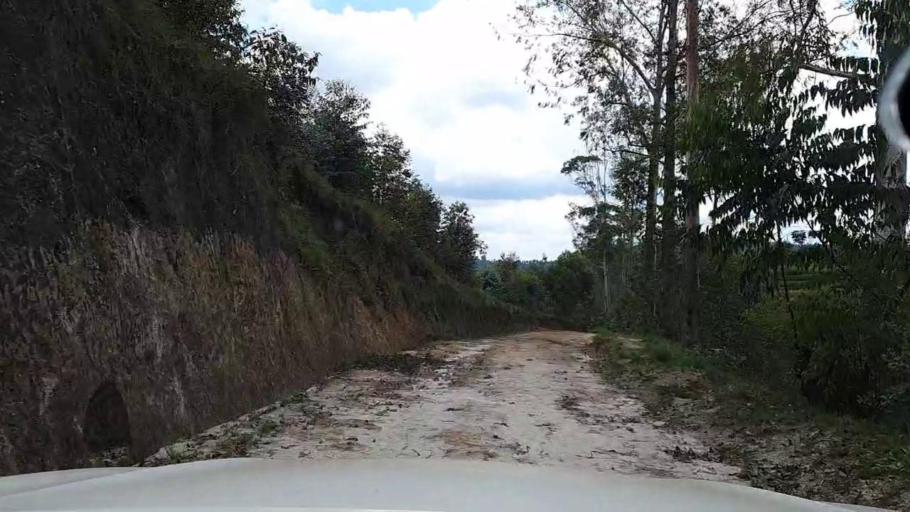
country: RW
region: Southern Province
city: Nzega
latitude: -2.6396
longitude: 29.4794
